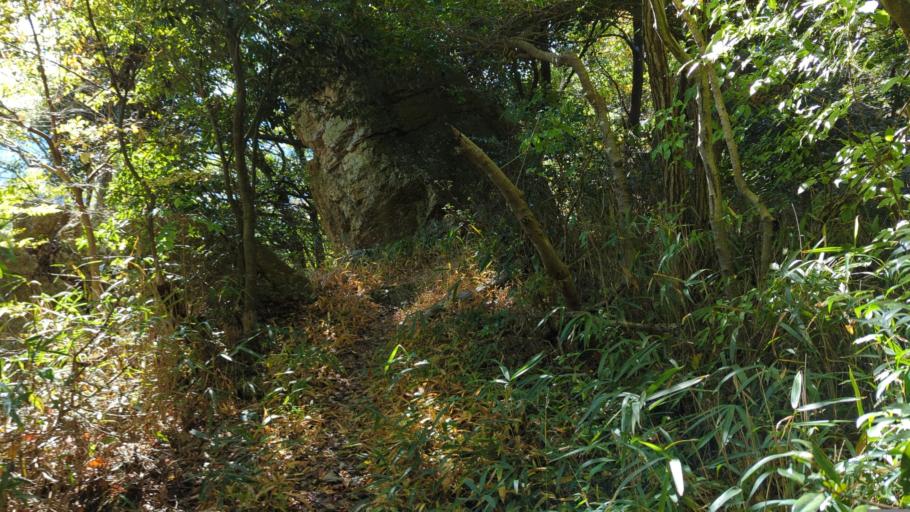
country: JP
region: Aichi
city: Toyohashi
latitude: 34.7698
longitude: 137.4406
